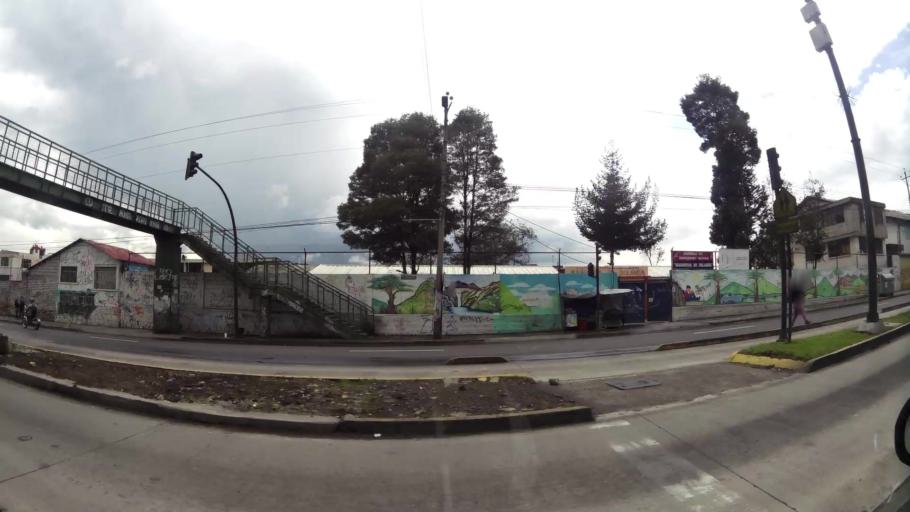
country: EC
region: Pichincha
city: Quito
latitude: -0.2733
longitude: -78.5524
